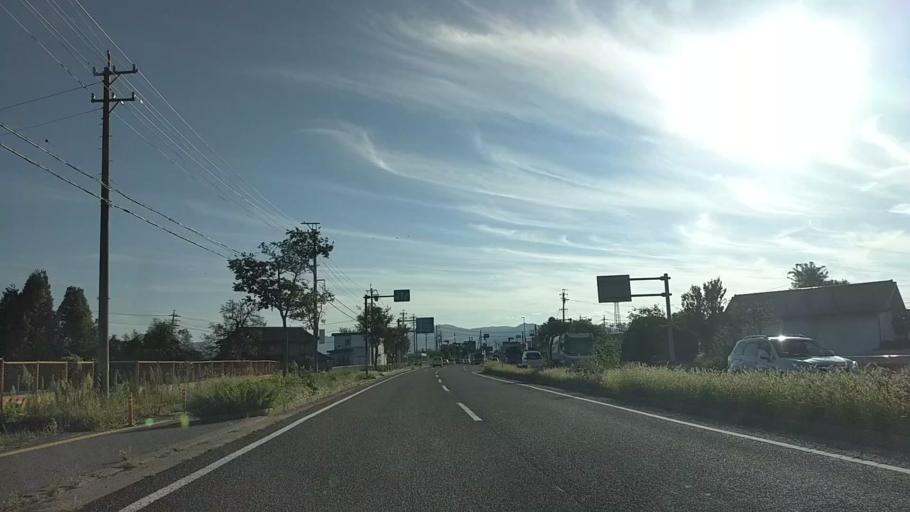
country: JP
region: Nagano
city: Nagano-shi
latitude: 36.5963
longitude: 138.1897
